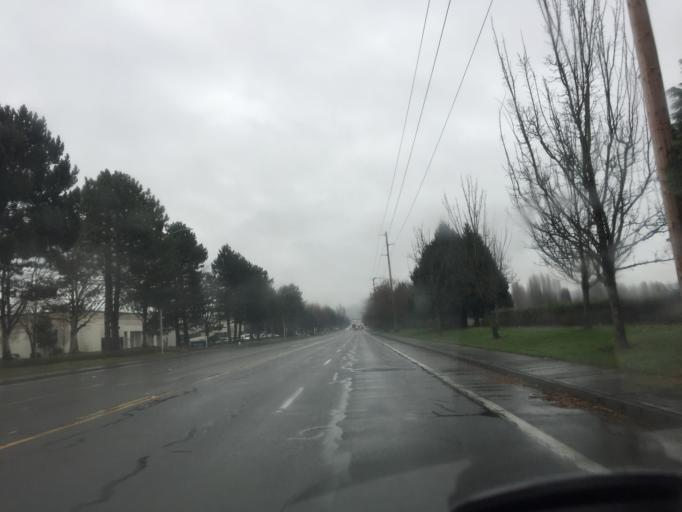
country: US
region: Washington
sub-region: King County
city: SeaTac
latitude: 47.4267
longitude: -122.2558
